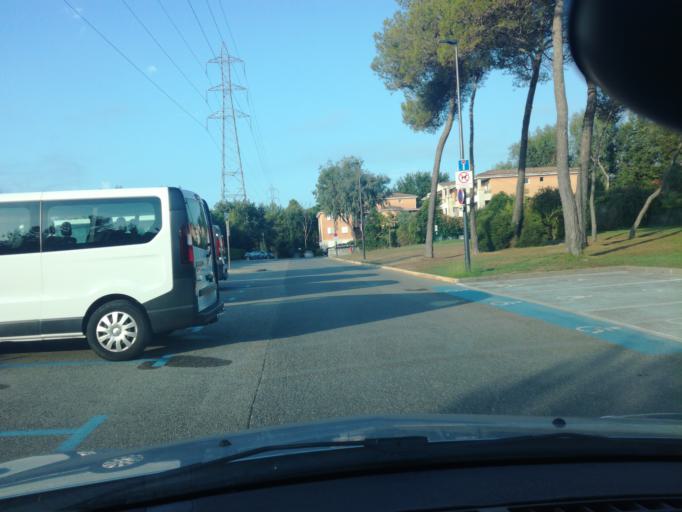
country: FR
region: Provence-Alpes-Cote d'Azur
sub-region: Departement des Alpes-Maritimes
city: Mougins
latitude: 43.6094
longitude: 7.0152
